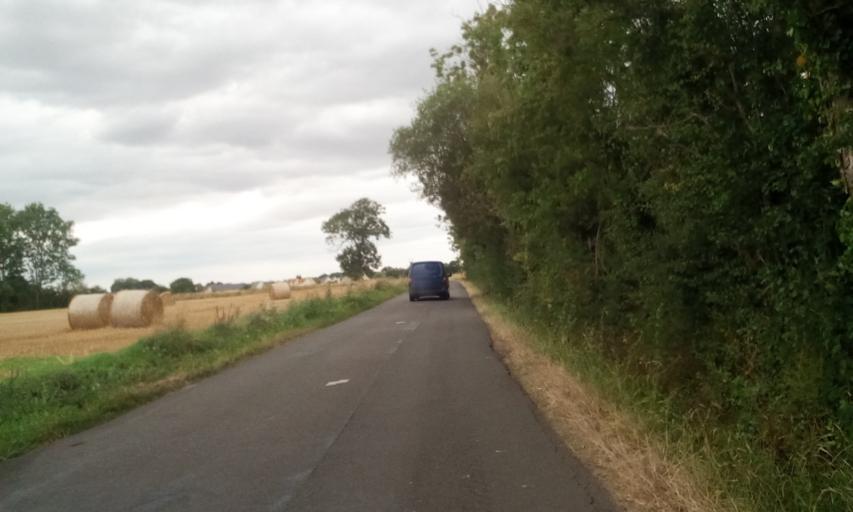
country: FR
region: Lower Normandy
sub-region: Departement du Calvados
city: Bellengreville
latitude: 49.1461
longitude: -0.2174
